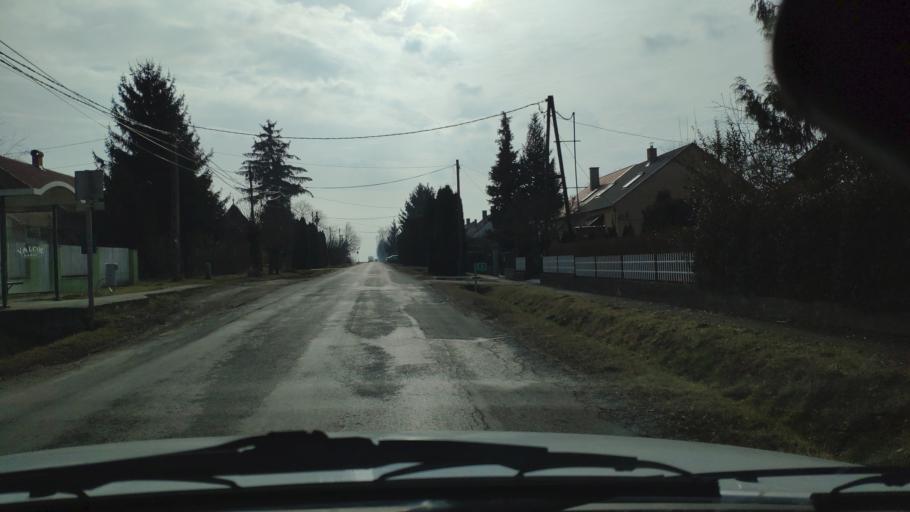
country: HU
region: Zala
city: Nagykanizsa
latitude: 46.4527
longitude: 16.9133
